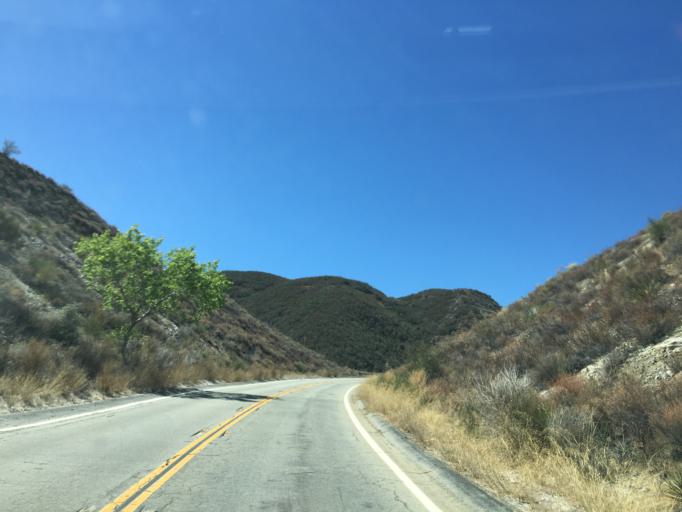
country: US
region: California
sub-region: Los Angeles County
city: Castaic
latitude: 34.5648
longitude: -118.5554
